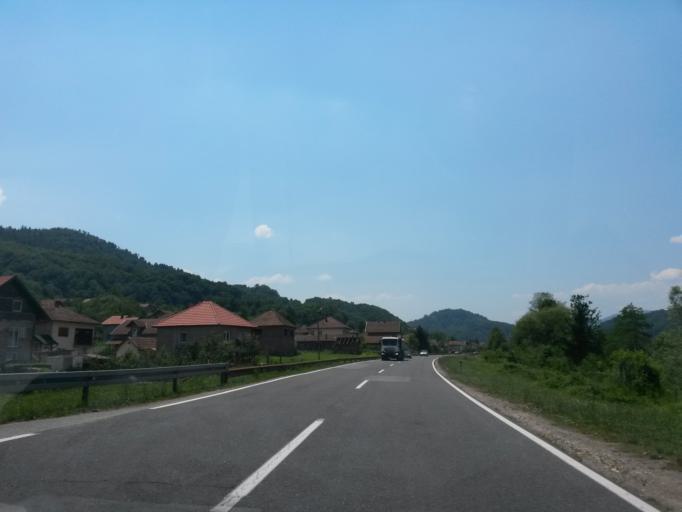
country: BA
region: Federation of Bosnia and Herzegovina
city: Maglaj
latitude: 44.5233
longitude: 18.0938
